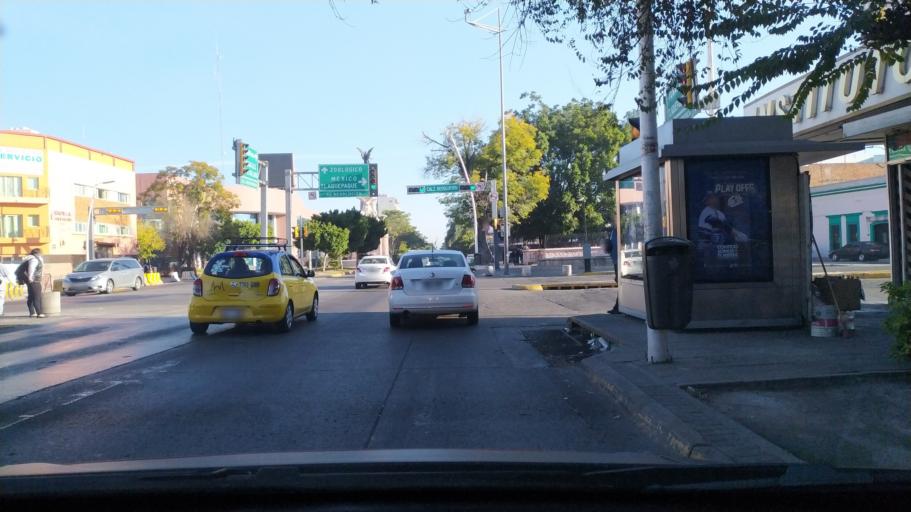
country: MX
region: Jalisco
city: Guadalajara
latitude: 20.6705
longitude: -103.3443
